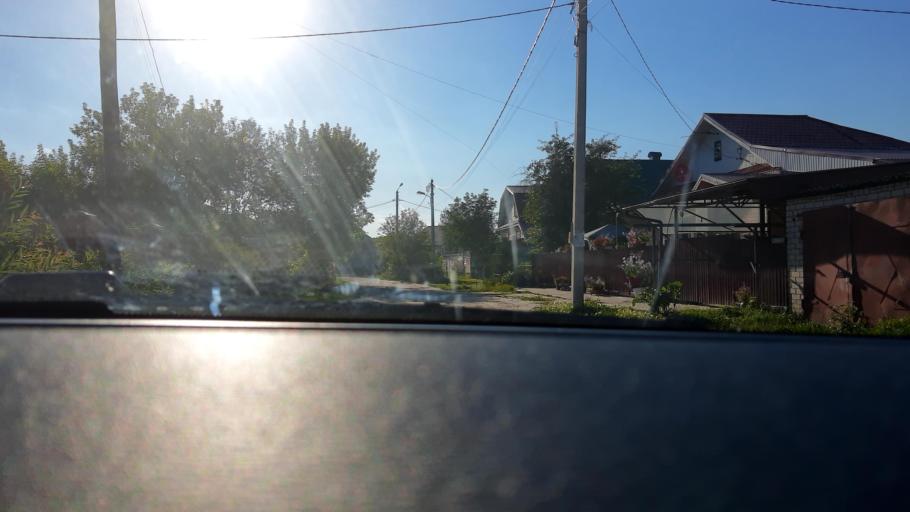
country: RU
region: Nizjnij Novgorod
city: Neklyudovo
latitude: 56.4058
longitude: 44.0350
